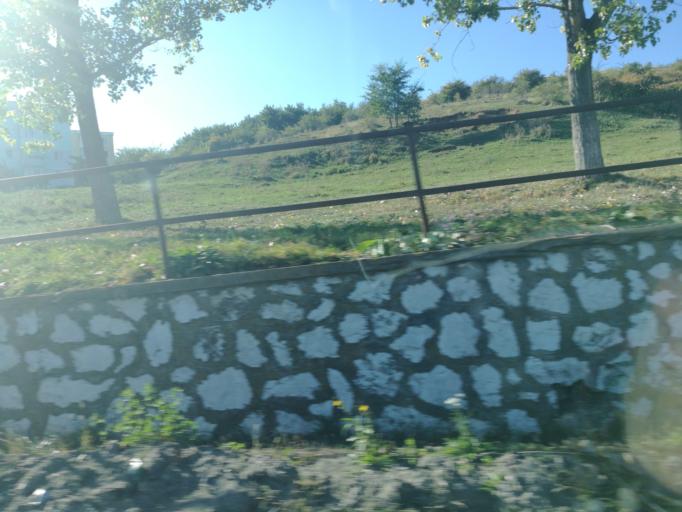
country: RO
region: Brasov
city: Codlea
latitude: 45.7082
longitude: 25.4531
